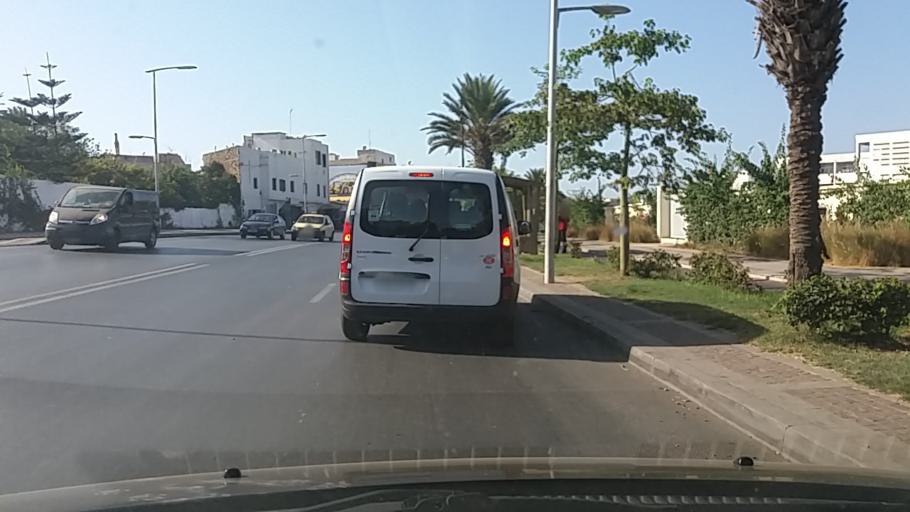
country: MA
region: Rabat-Sale-Zemmour-Zaer
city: Sale
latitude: 34.0439
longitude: -6.8177
